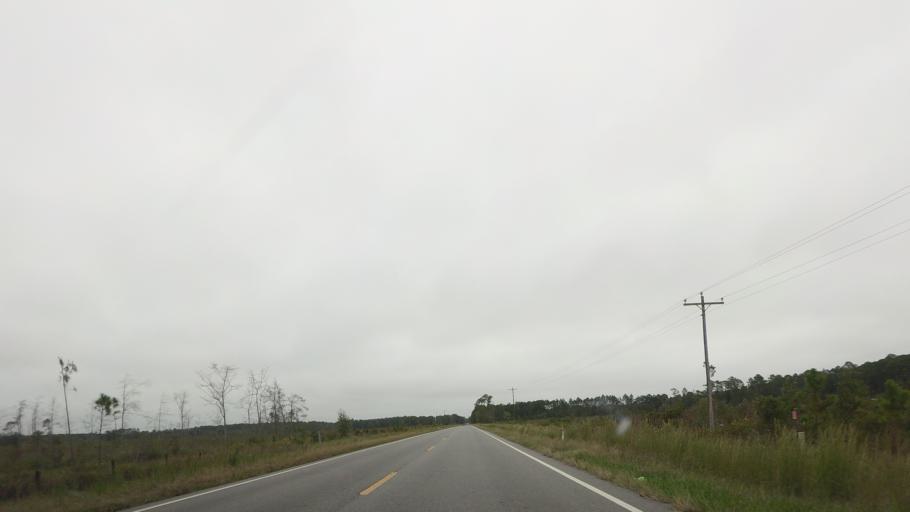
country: US
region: Georgia
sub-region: Berrien County
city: Enigma
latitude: 31.3606
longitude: -83.2272
